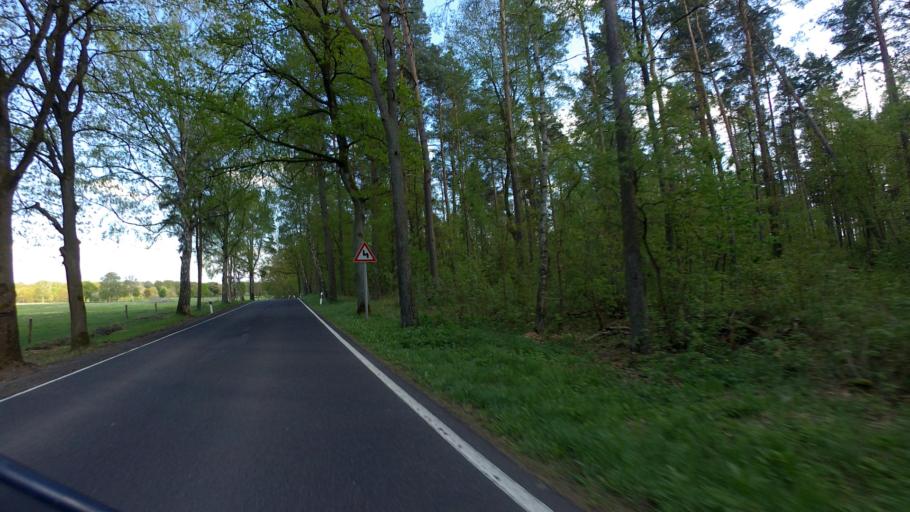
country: DE
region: Brandenburg
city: Templin
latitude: 53.0509
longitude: 13.5467
